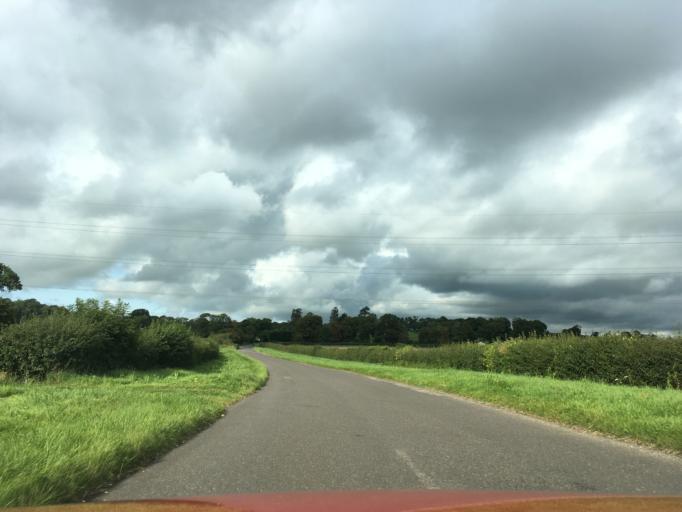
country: GB
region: England
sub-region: South Gloucestershire
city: Tytherington
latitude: 51.6174
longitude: -2.4834
